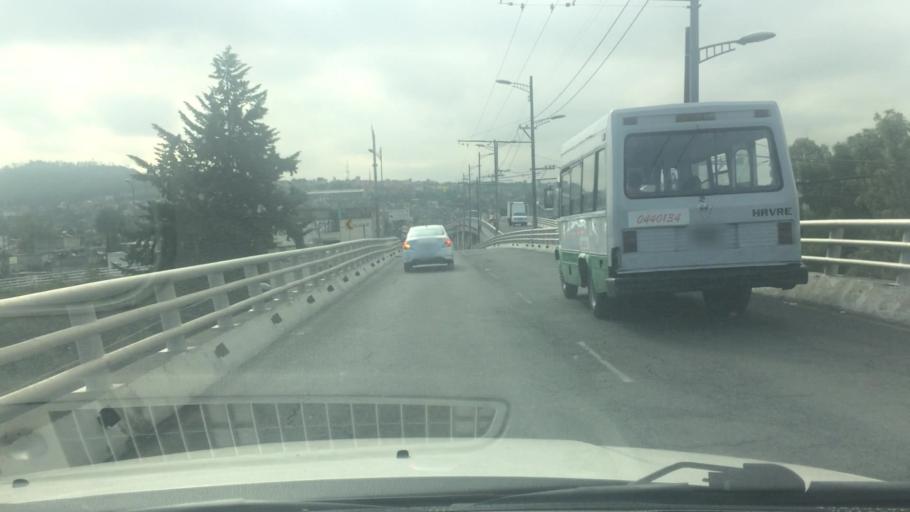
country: MX
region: Mexico City
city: Colonia Nativitas
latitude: 19.3390
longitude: -99.1138
